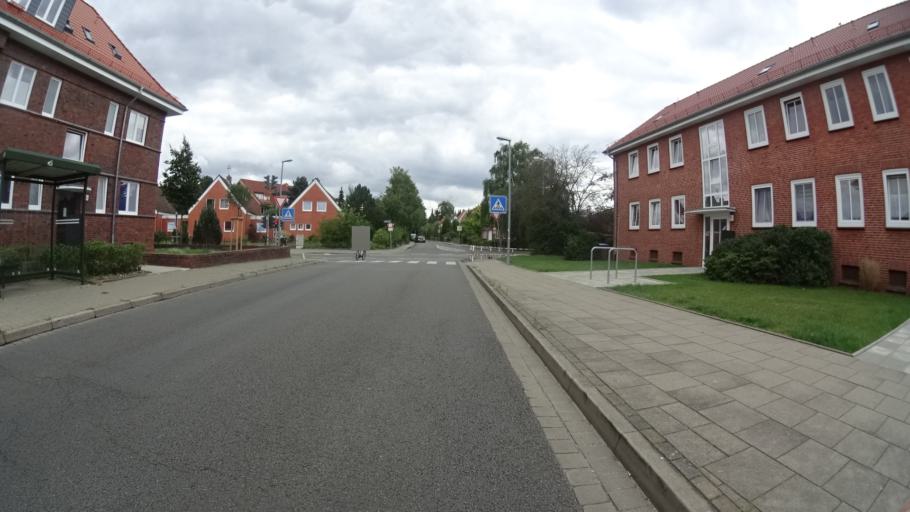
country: DE
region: Lower Saxony
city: Lueneburg
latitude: 53.2359
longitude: 10.3892
